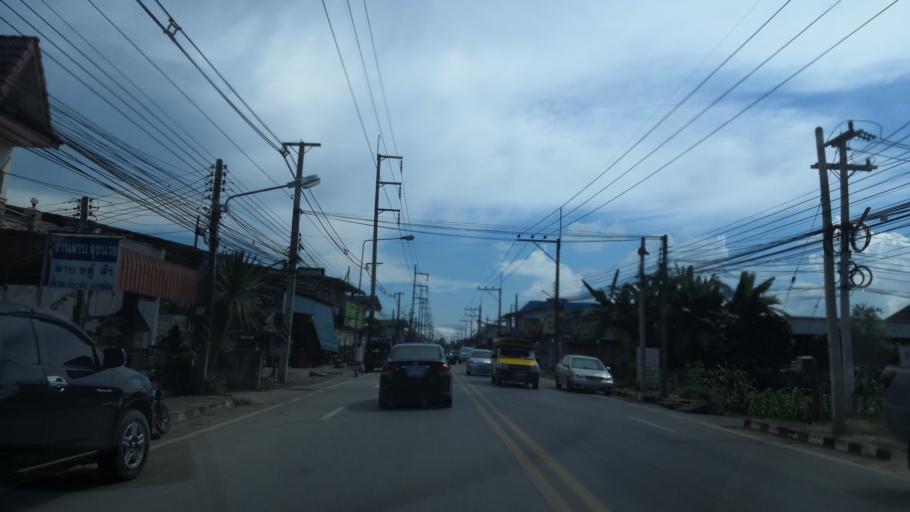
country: TH
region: Chiang Rai
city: Wiang Pa Pao
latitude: 19.3707
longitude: 99.5030
